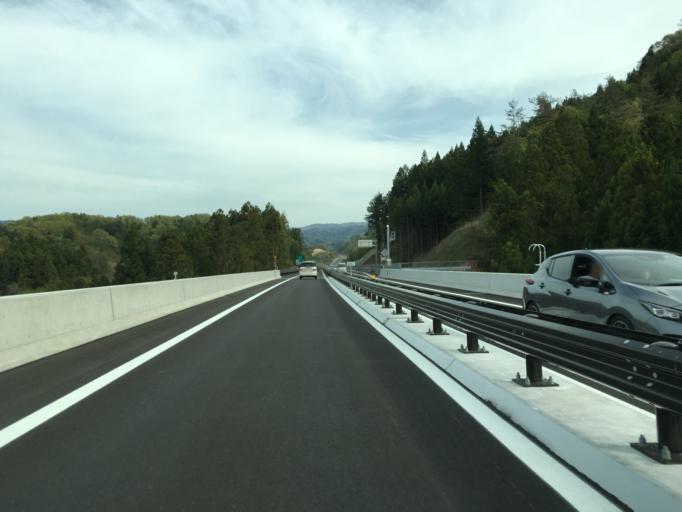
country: JP
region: Fukushima
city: Hobaramachi
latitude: 37.7762
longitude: 140.5818
